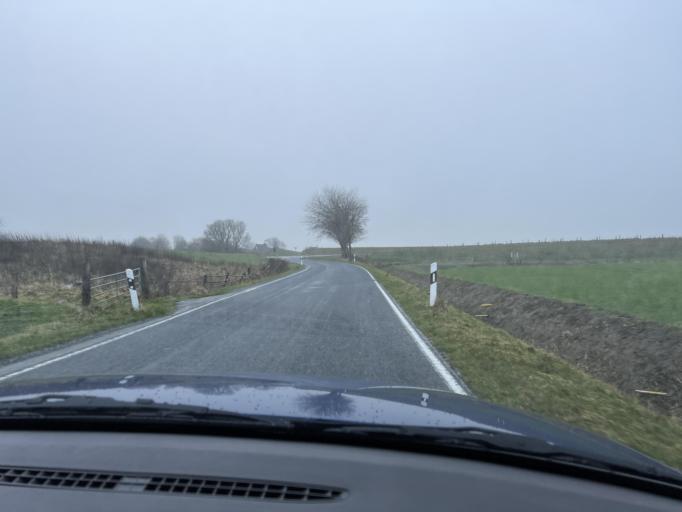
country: DE
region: Schleswig-Holstein
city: Schulp
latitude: 54.2661
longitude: 8.9358
